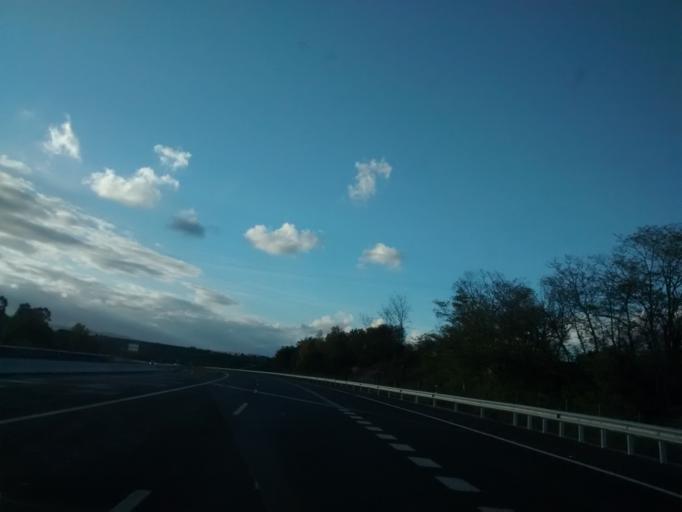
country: ES
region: Cantabria
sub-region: Provincia de Cantabria
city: Polanco
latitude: 43.3455
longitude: -3.9973
